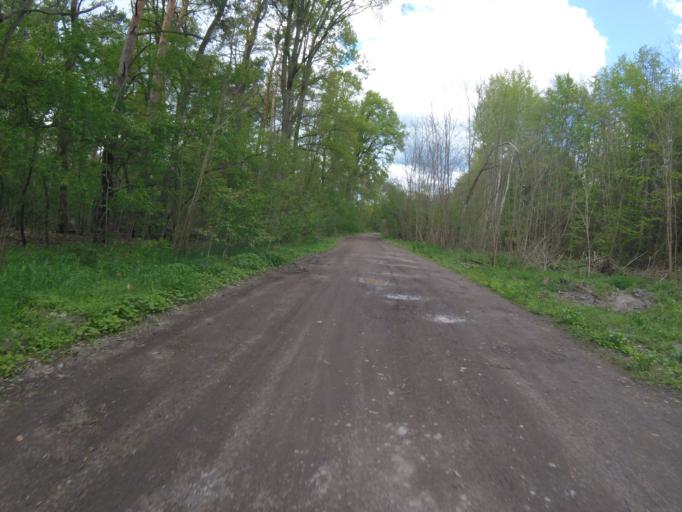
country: DE
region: Brandenburg
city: Schwerin
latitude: 52.1710
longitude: 13.5949
